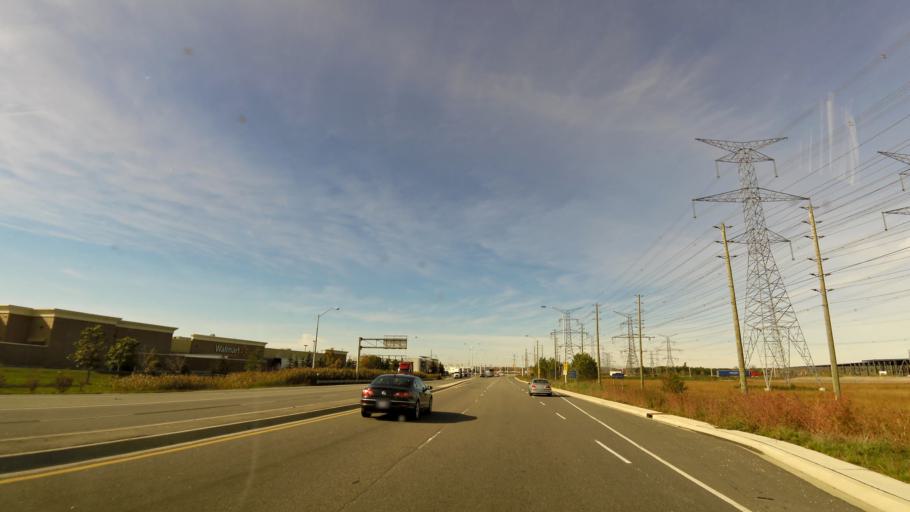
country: CA
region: Ontario
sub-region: Halton
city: Milton
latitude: 43.5430
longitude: -79.8651
